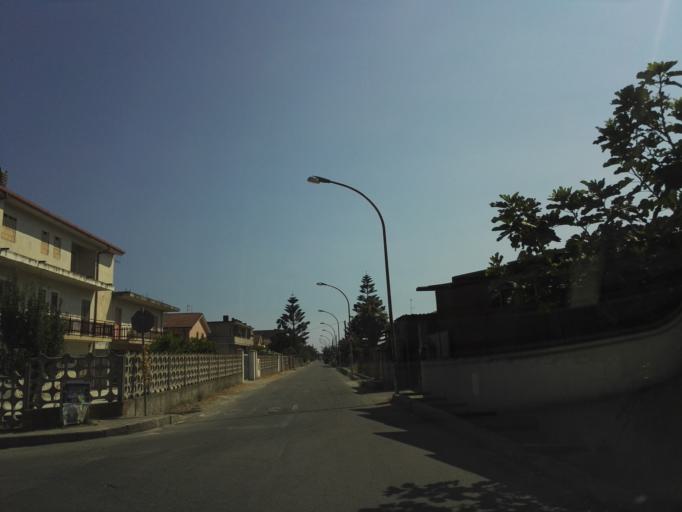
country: IT
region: Calabria
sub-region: Provincia di Reggio Calabria
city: Monasterace Marina
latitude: 38.4335
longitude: 16.5701
